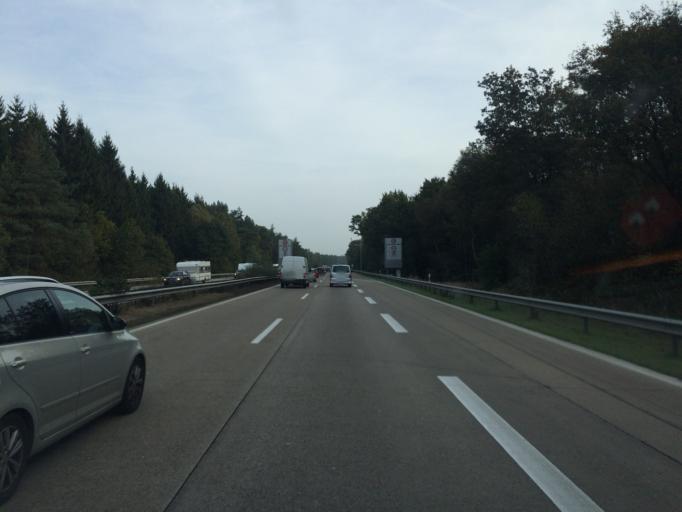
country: DE
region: Lower Saxony
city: Soltau
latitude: 52.9082
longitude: 9.7932
